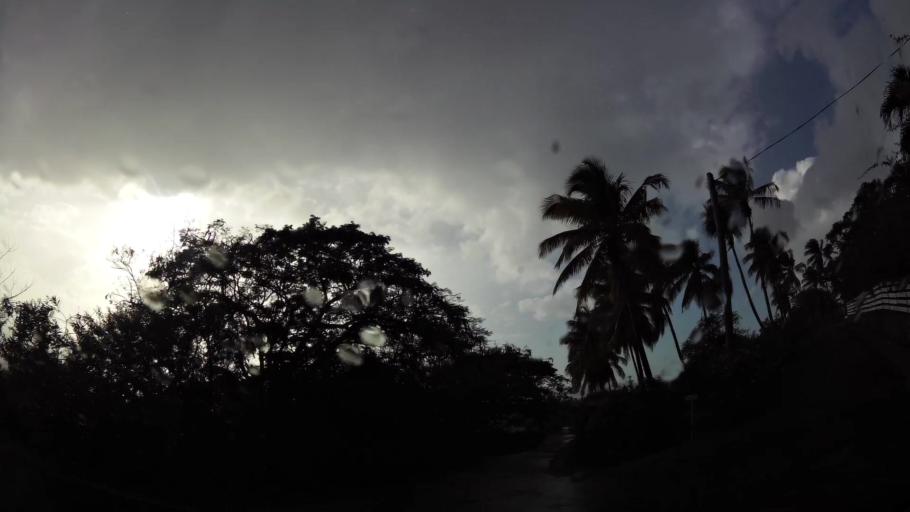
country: DM
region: Saint Paul
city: Mahaut
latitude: 15.3654
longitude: -61.3997
